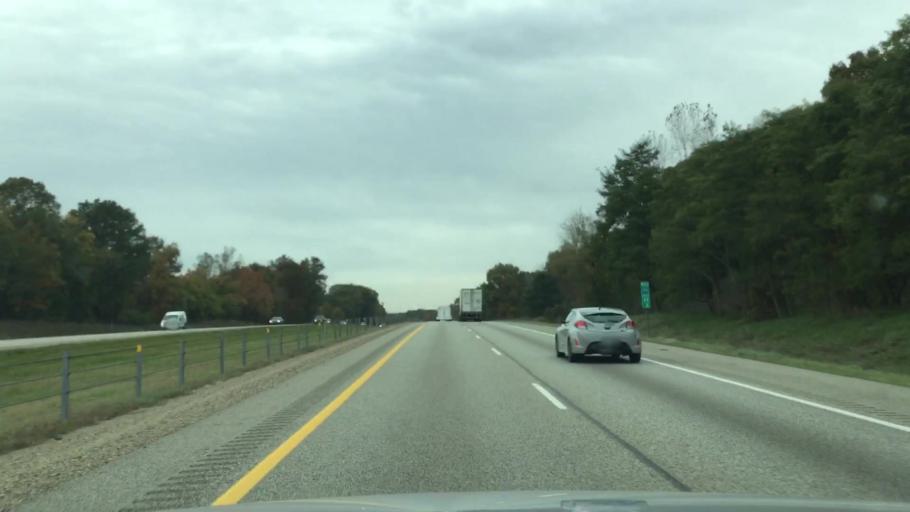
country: US
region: Michigan
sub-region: Kalamazoo County
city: Galesburg
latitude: 42.2808
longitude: -85.3383
